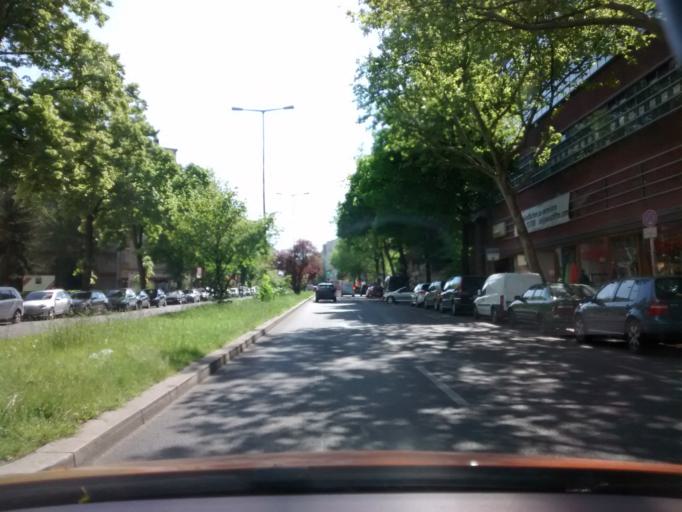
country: DE
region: Berlin
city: Friedenau
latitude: 52.4732
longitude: 13.3371
